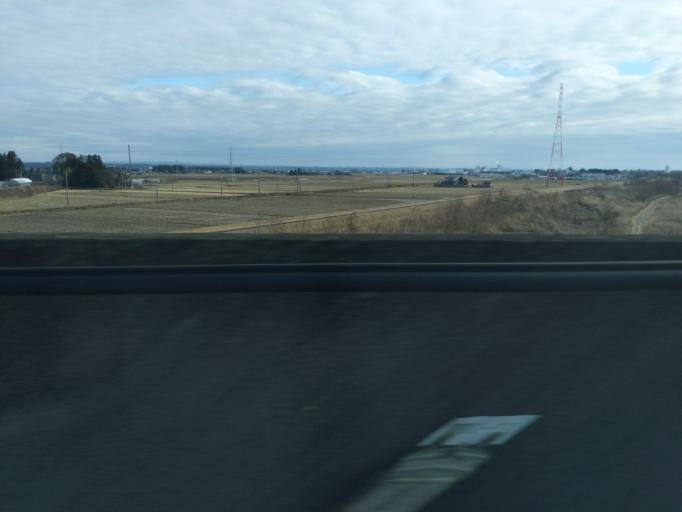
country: JP
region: Tochigi
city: Ujiie
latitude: 36.7096
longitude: 139.9226
